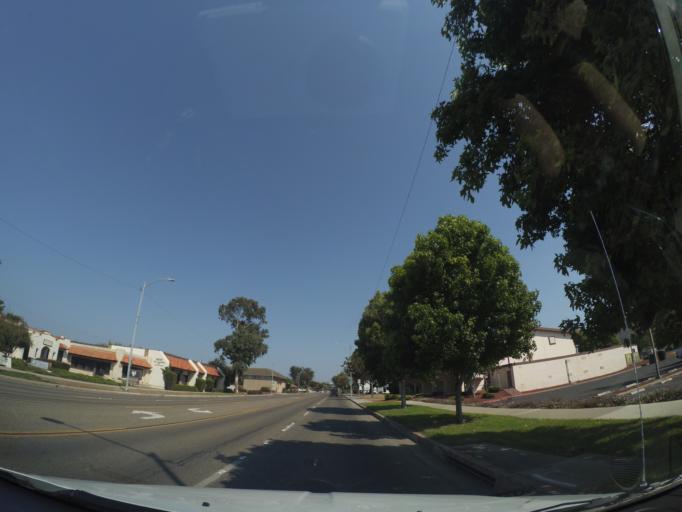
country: US
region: California
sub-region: Santa Barbara County
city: Lompoc
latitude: 34.6389
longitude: -120.4527
